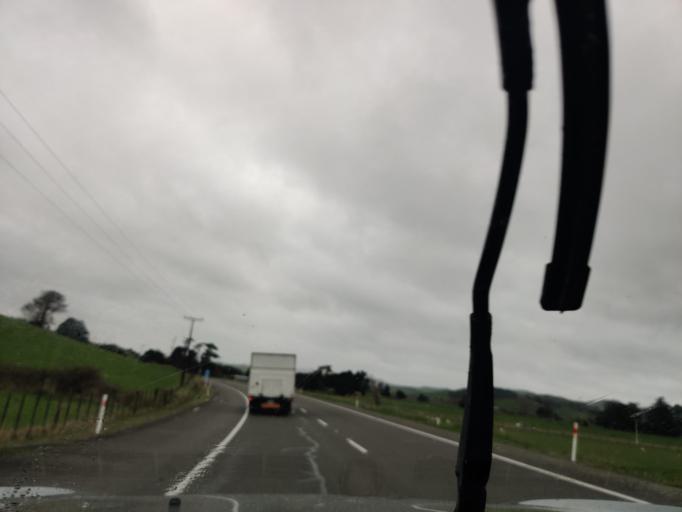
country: NZ
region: Manawatu-Wanganui
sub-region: Palmerston North City
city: Palmerston North
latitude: -40.3412
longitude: 175.8847
